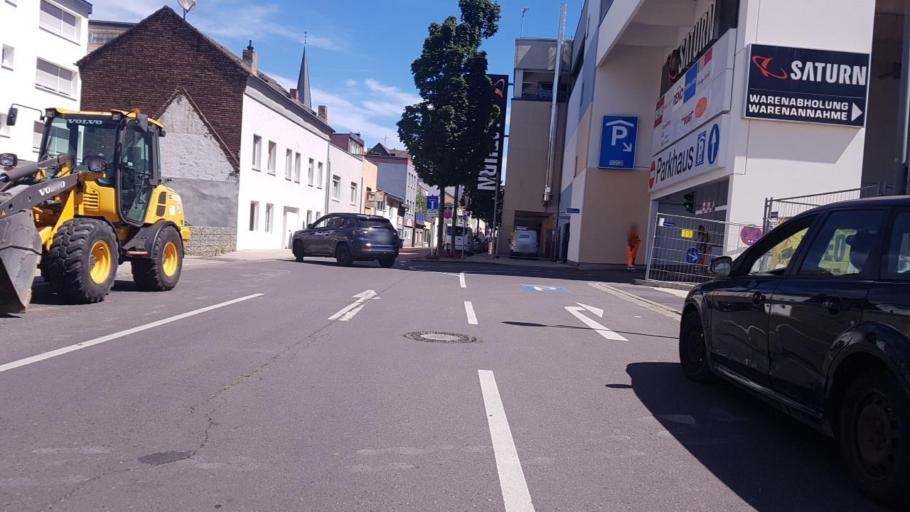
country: DE
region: North Rhine-Westphalia
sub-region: Regierungsbezirk Koln
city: Euskirchen
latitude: 50.6584
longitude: 6.7892
